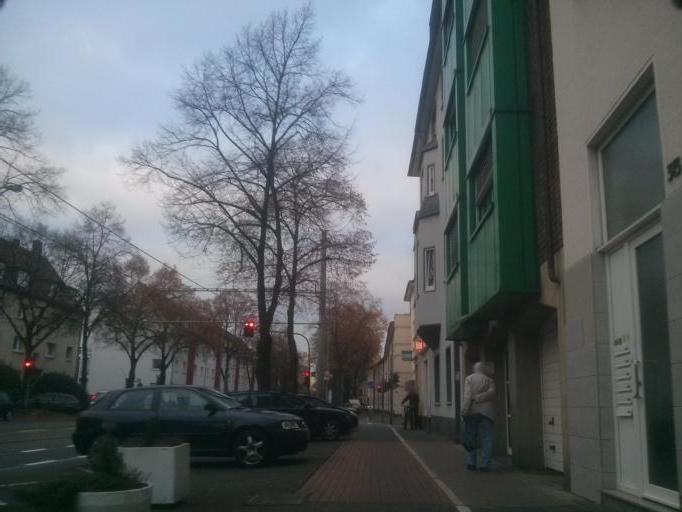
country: DE
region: North Rhine-Westphalia
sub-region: Regierungsbezirk Koln
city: Poll
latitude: 50.9181
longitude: 6.9888
